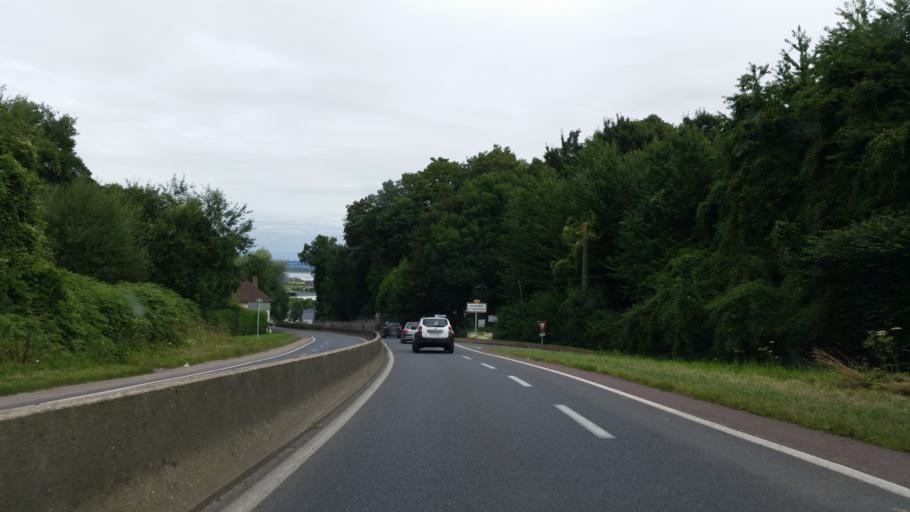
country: FR
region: Lower Normandy
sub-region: Departement du Calvados
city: La Riviere-Saint-Sauveur
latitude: 49.4056
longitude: 0.2524
